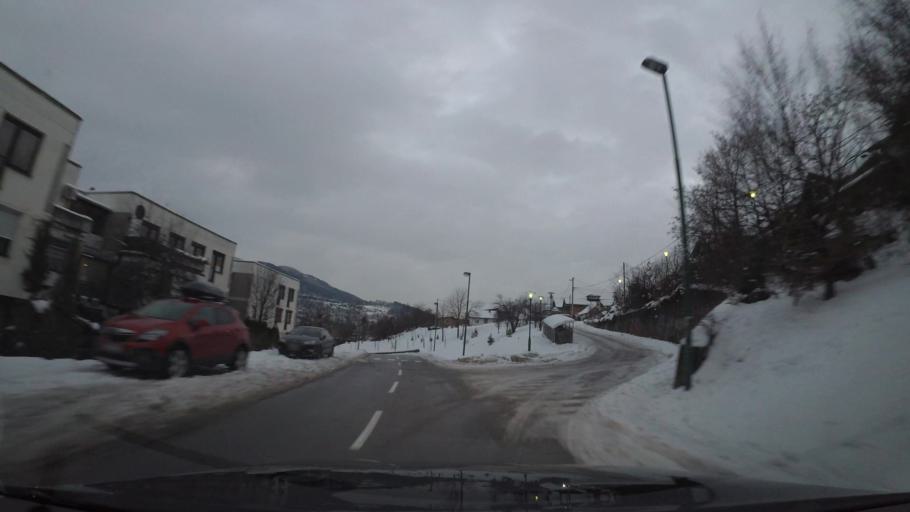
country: BA
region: Federation of Bosnia and Herzegovina
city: Kobilja Glava
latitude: 43.8639
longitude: 18.4071
